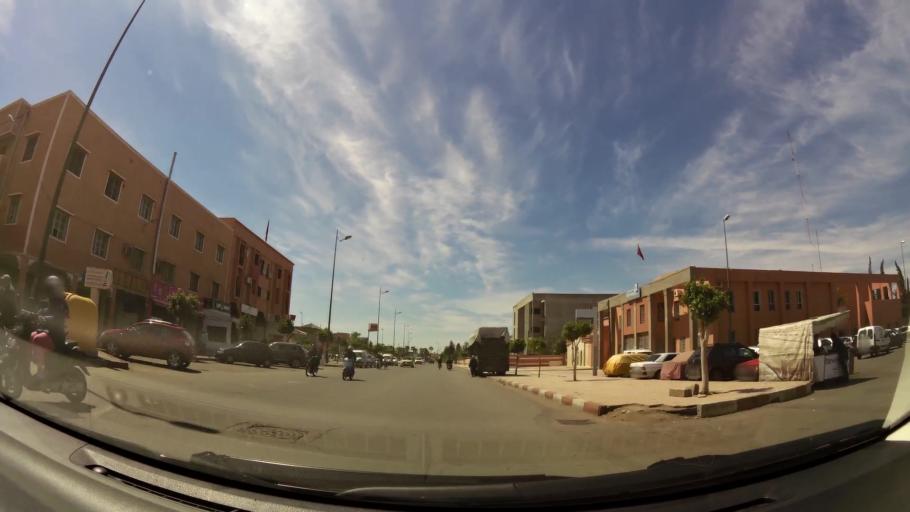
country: MA
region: Marrakech-Tensift-Al Haouz
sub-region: Marrakech
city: Marrakesh
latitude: 31.6135
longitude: -7.9716
